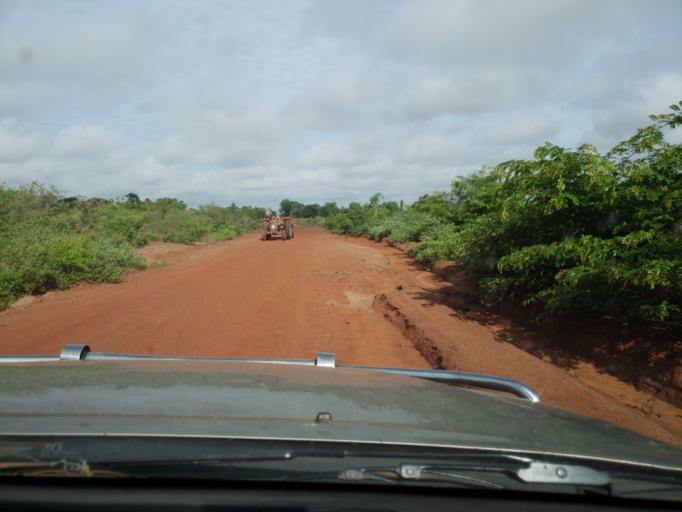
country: ML
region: Sikasso
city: Koutiala
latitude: 12.3930
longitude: -5.9836
